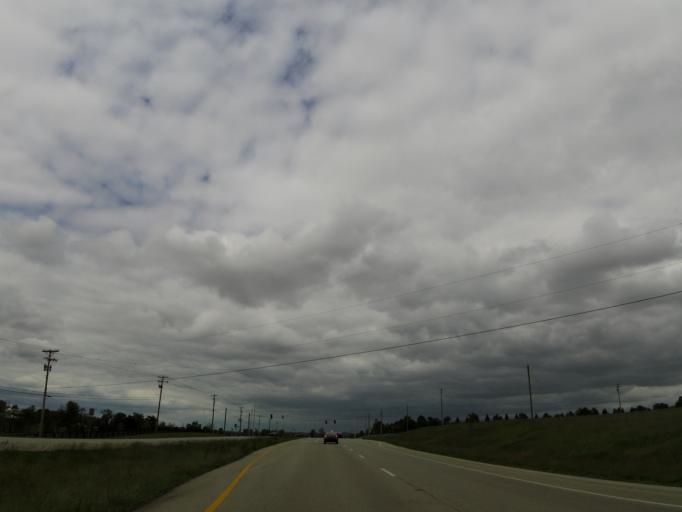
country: US
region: Kentucky
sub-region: Scott County
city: Georgetown
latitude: 38.1699
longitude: -84.6012
